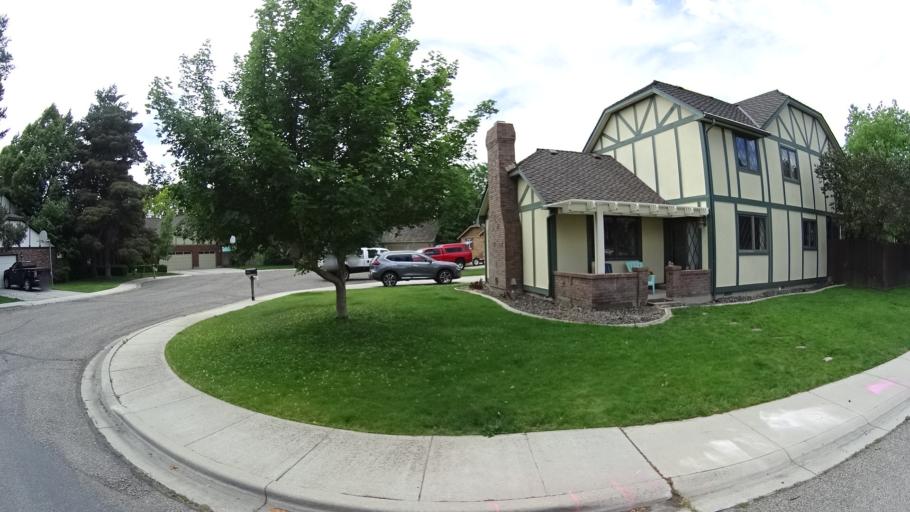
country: US
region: Idaho
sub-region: Ada County
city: Eagle
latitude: 43.6455
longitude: -116.3326
